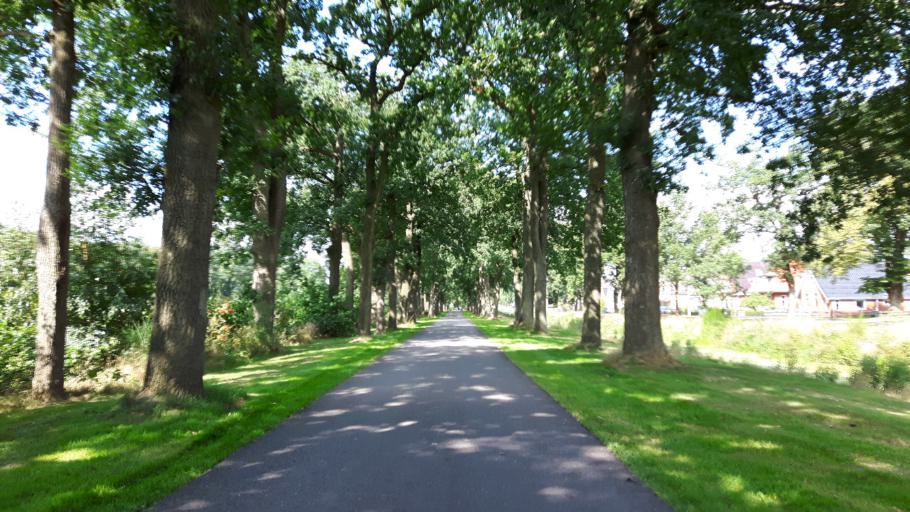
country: NL
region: Friesland
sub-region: Gemeente Smallingerland
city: Drachtstercompagnie
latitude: 53.0772
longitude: 6.2603
